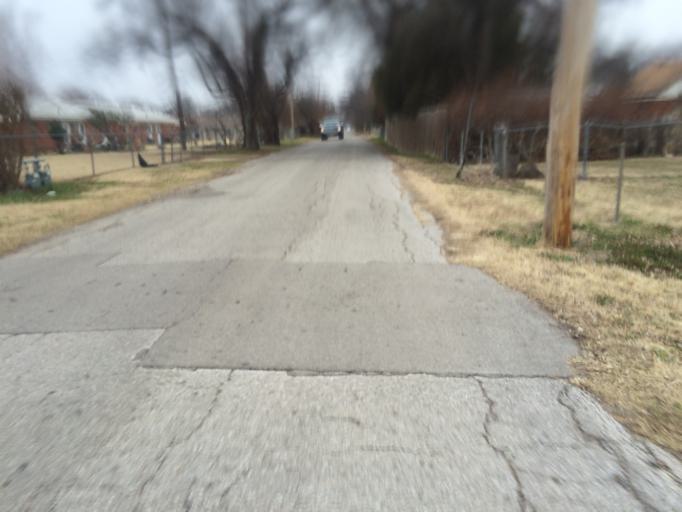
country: US
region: Oklahoma
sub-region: Cleveland County
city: Norman
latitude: 35.2044
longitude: -97.4280
